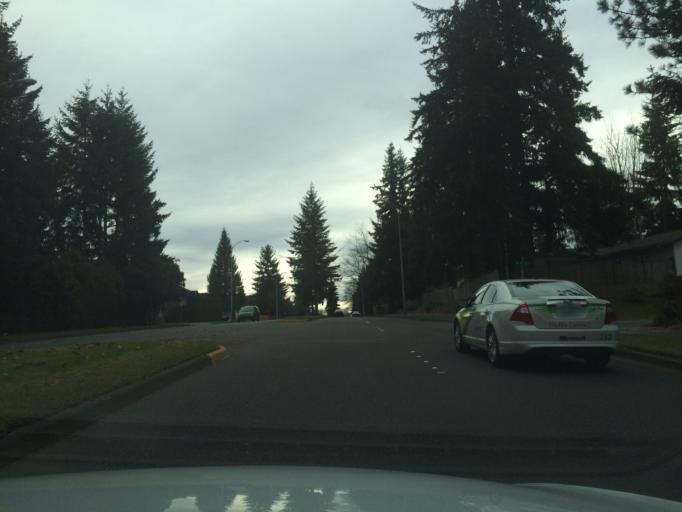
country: US
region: Washington
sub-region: King County
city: Redmond
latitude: 47.6643
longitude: -122.1433
